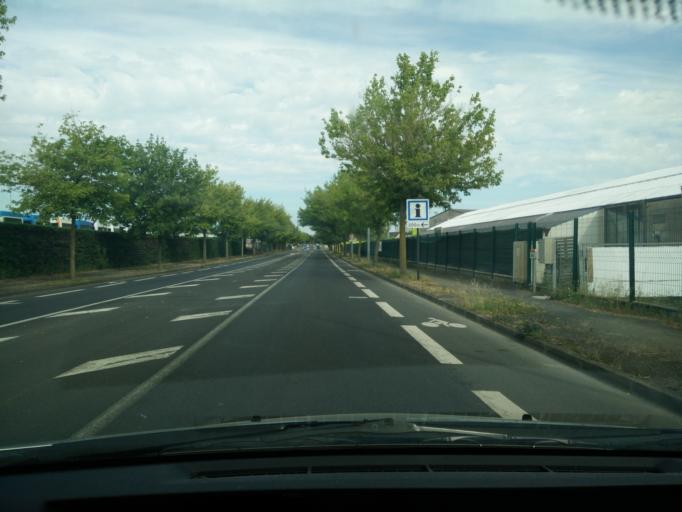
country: FR
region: Pays de la Loire
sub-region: Departement de Maine-et-Loire
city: Les Ponts-de-Ce
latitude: 47.4352
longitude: -0.5007
